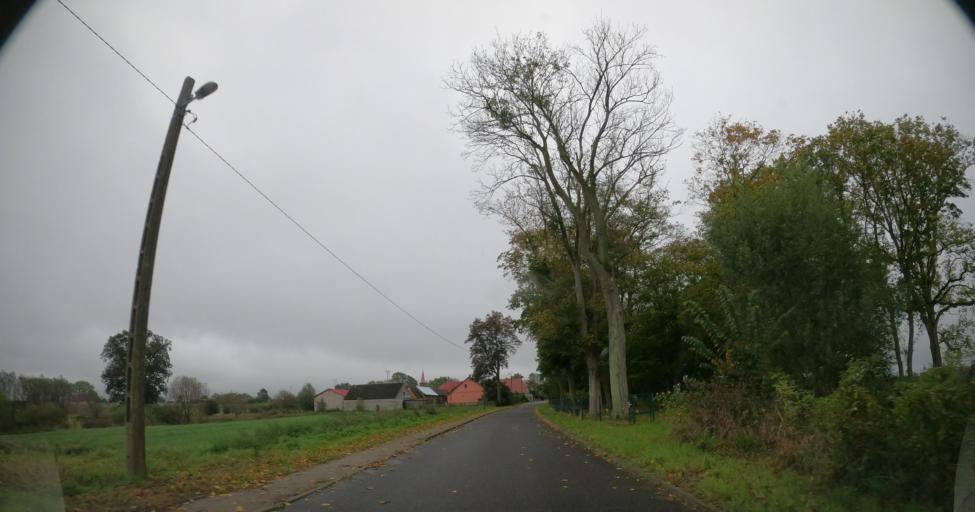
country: PL
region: West Pomeranian Voivodeship
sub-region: Powiat pyrzycki
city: Kozielice
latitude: 53.0958
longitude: 14.7679
